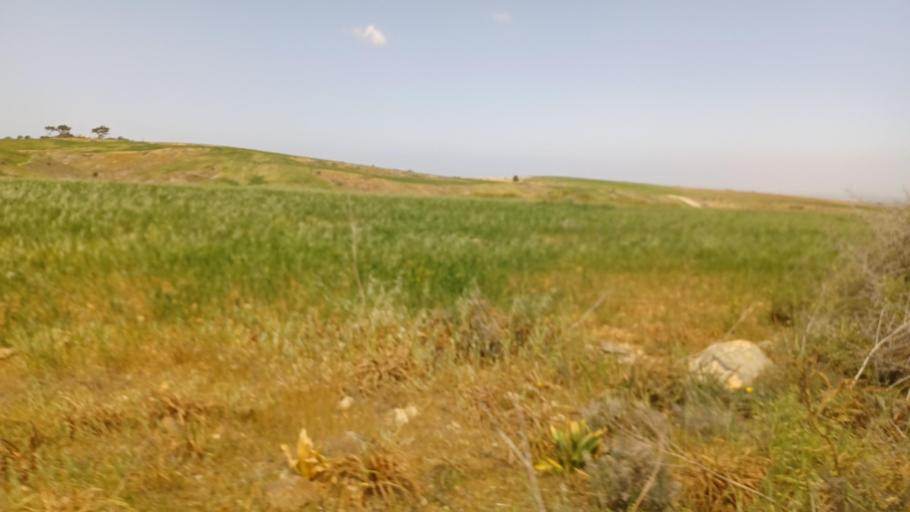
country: CY
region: Lefkosia
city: Lefka
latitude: 35.0922
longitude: 32.9309
